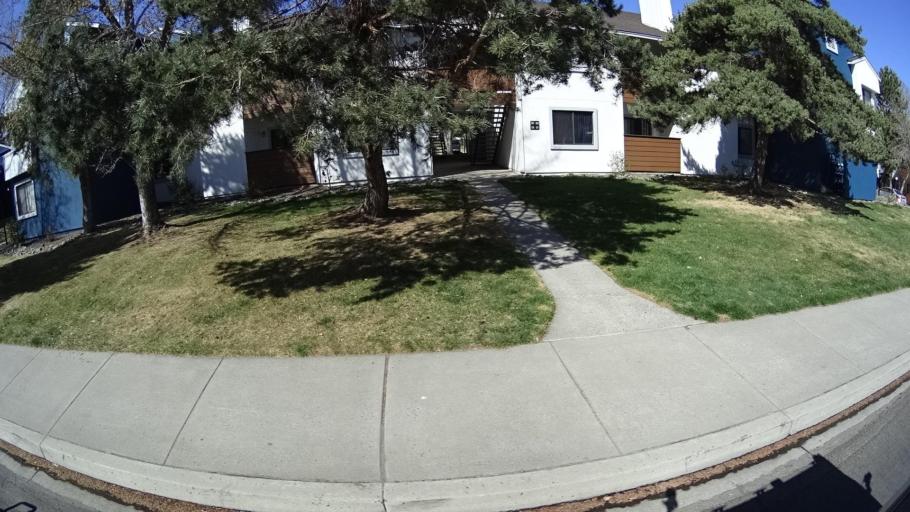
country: US
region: Nevada
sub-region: Washoe County
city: Reno
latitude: 39.4791
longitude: -119.8005
